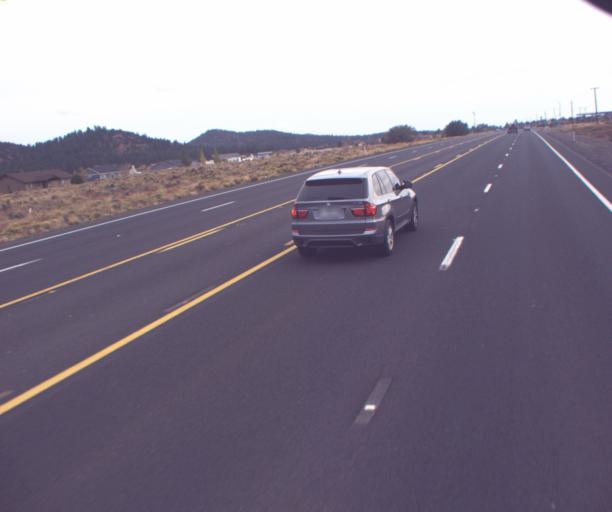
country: US
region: Arizona
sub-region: Coconino County
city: Flagstaff
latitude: 35.3054
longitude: -111.5428
